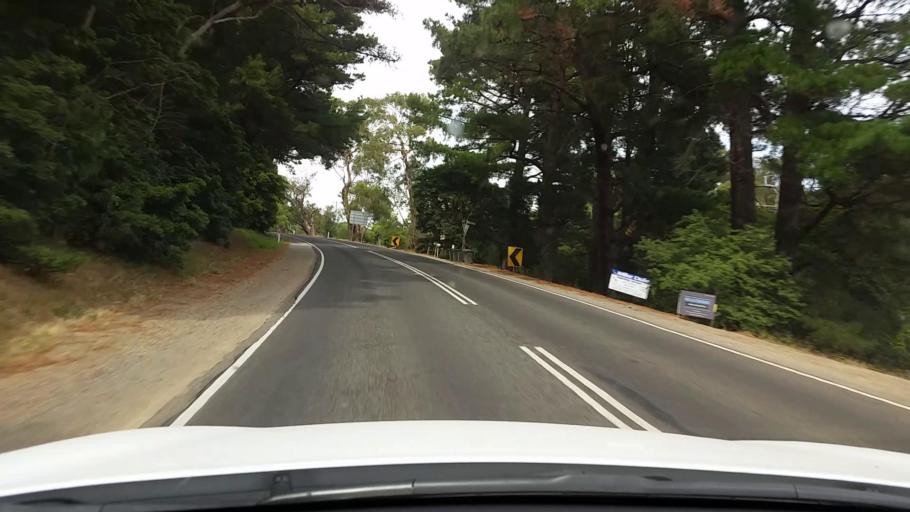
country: AU
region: Victoria
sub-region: Mornington Peninsula
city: Merricks
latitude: -38.3934
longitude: 145.0850
